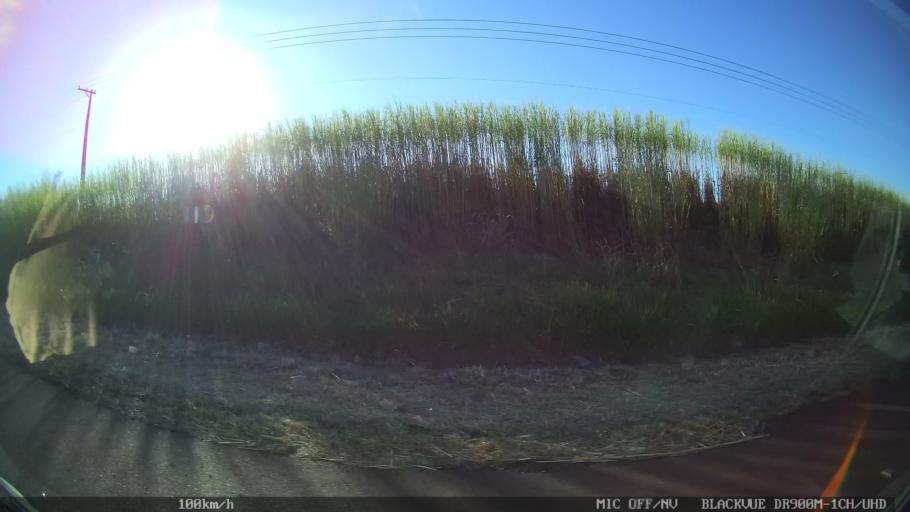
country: BR
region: Sao Paulo
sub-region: Olimpia
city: Olimpia
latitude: -20.7088
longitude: -48.9680
